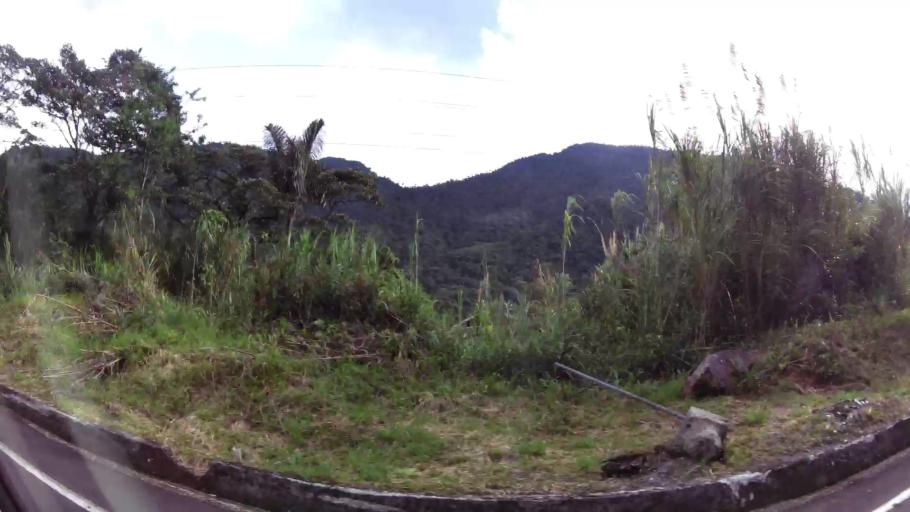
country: EC
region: Pastaza
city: Puyo
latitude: -1.4491
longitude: -78.1713
